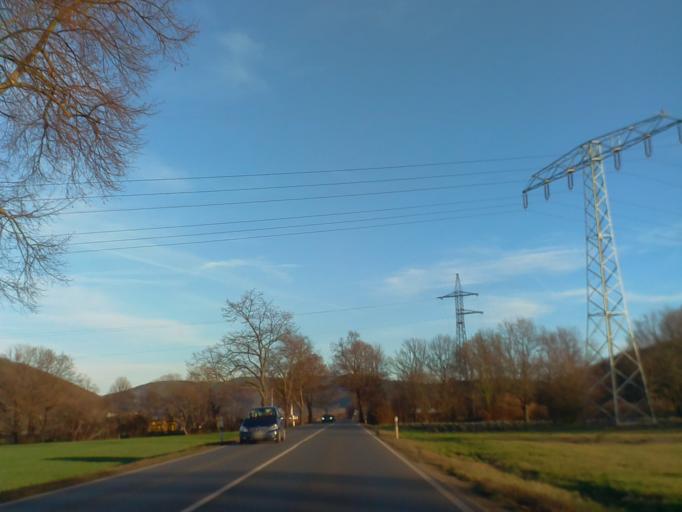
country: DE
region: Thuringia
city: Bad Blankenburg
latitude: 50.6846
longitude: 11.2927
